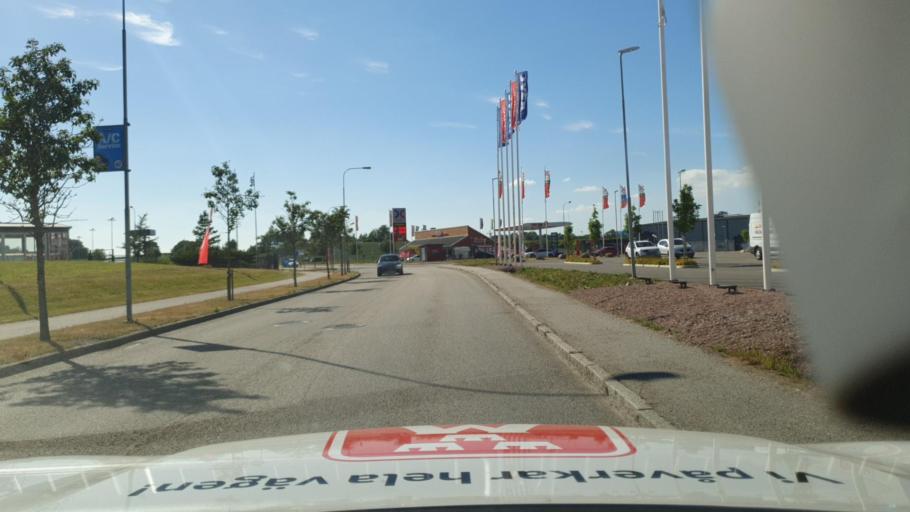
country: SE
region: Skane
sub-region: Skurups Kommun
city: Skurup
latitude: 55.4901
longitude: 13.4853
